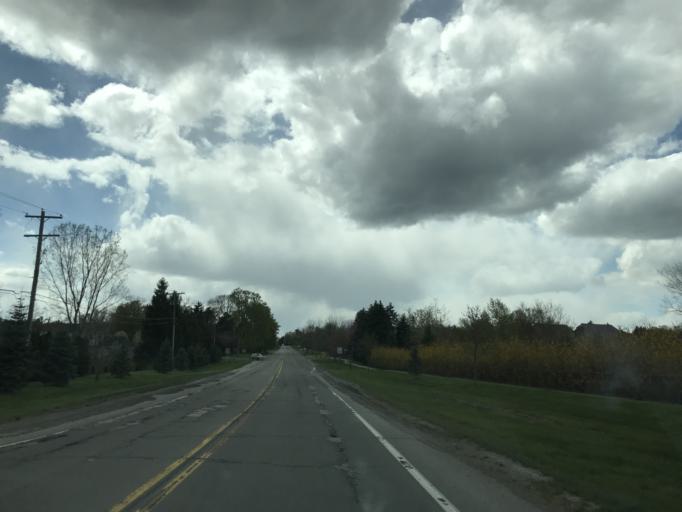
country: US
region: Michigan
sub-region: Wayne County
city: Plymouth
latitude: 42.3777
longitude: -83.4953
